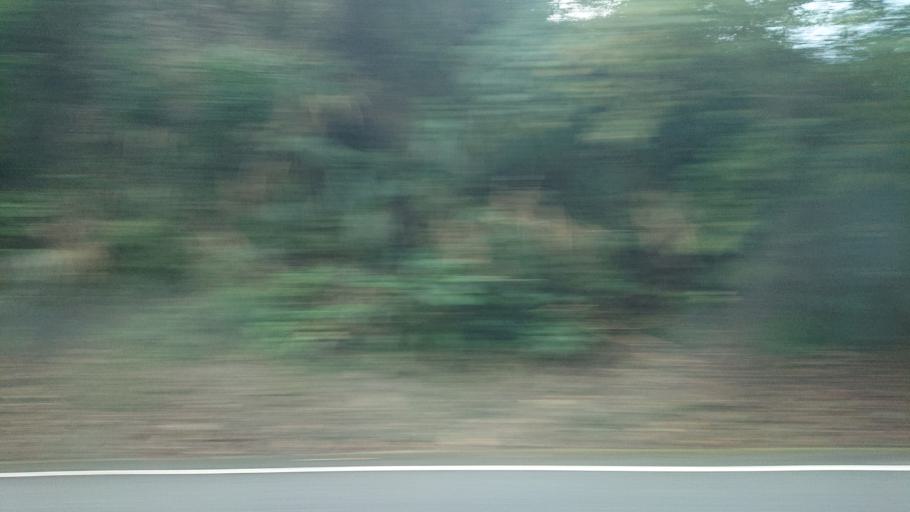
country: TW
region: Taiwan
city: Lugu
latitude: 23.4826
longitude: 120.7389
